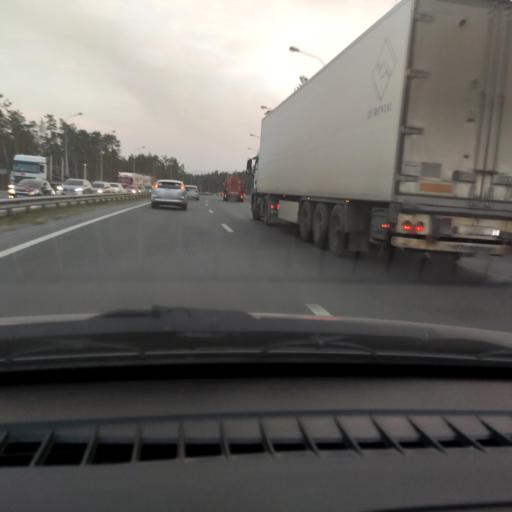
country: RU
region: Samara
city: Zhigulevsk
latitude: 53.5383
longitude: 49.5166
